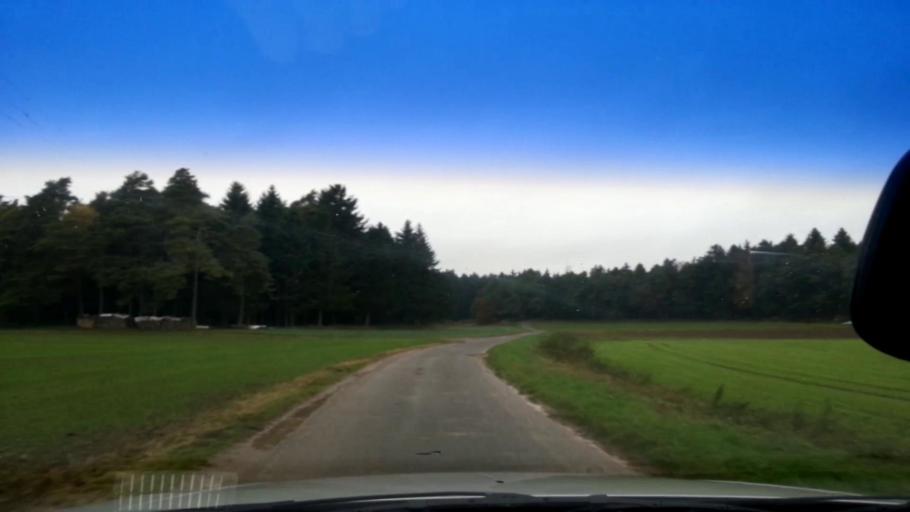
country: DE
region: Bavaria
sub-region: Upper Franconia
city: Wattendorf
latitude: 50.0147
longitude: 11.1499
